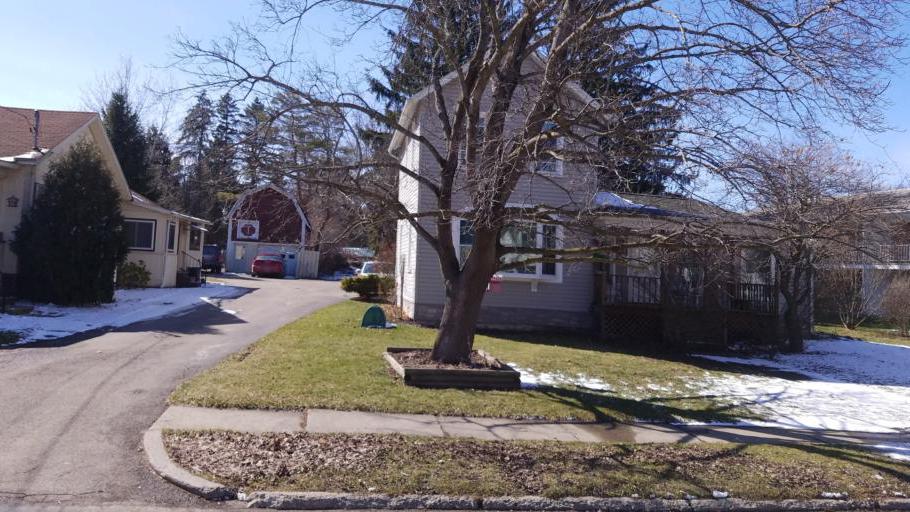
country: US
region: New York
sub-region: Allegany County
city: Wellsville
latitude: 42.1148
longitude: -77.9485
